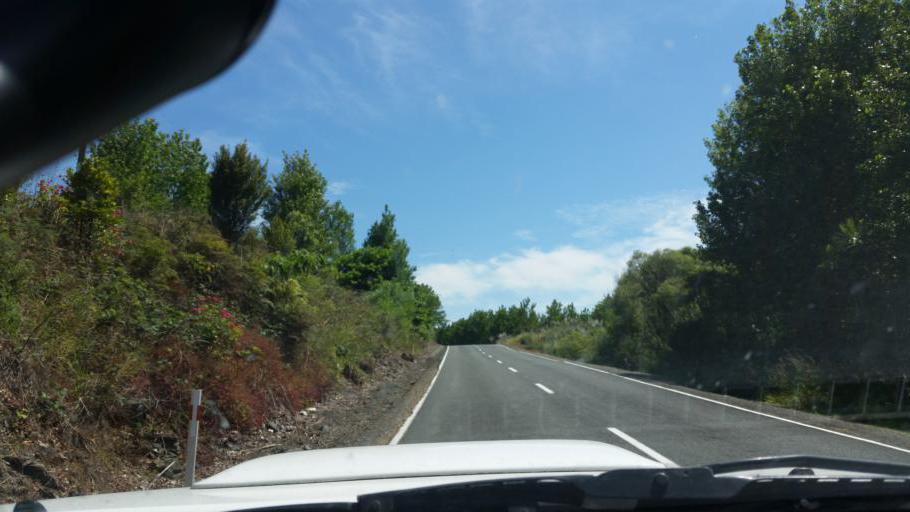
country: NZ
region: Auckland
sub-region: Auckland
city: Wellsford
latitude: -36.2131
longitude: 174.3908
